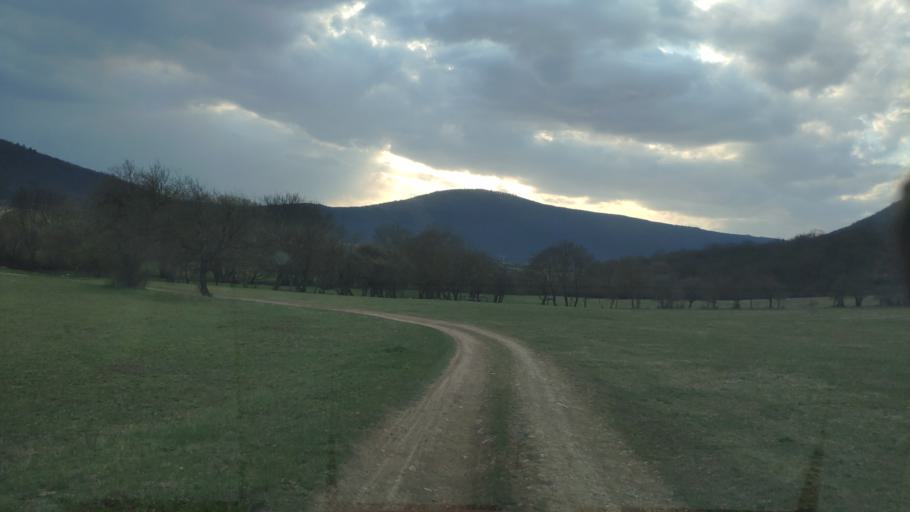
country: SK
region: Kosicky
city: Medzev
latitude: 48.6228
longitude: 20.8930
